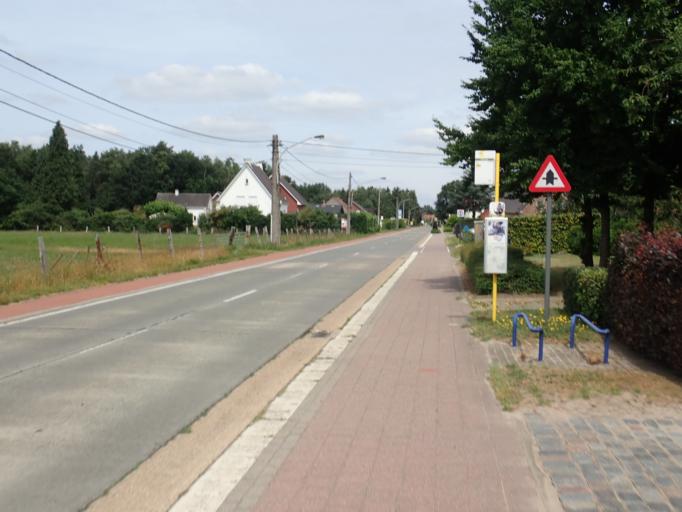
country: BE
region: Flanders
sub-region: Provincie Antwerpen
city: Rijkevorsel
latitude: 51.3157
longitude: 4.7760
